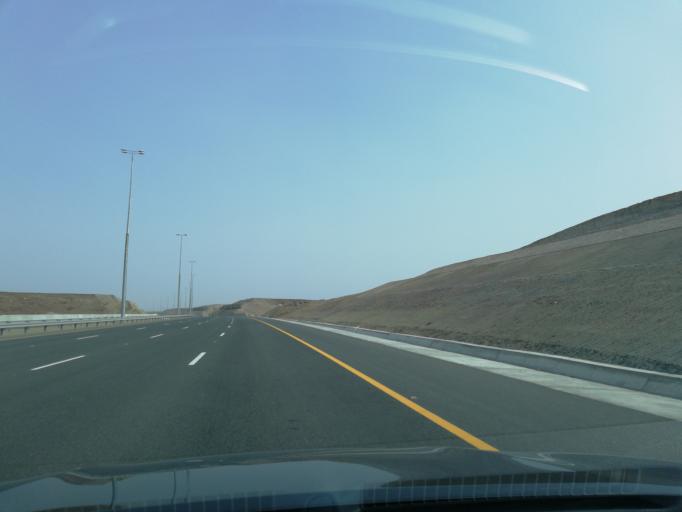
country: OM
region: Al Batinah
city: Al Liwa'
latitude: 24.3469
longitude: 56.5495
